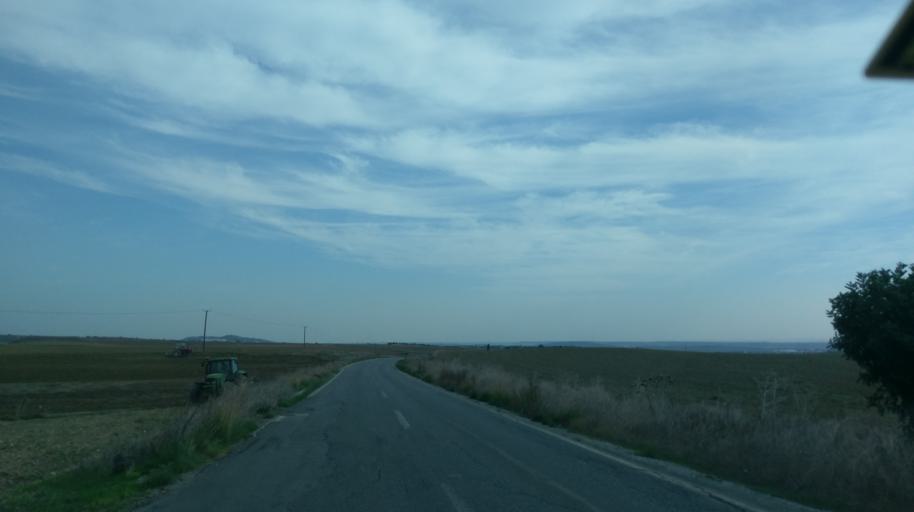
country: CY
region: Keryneia
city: Lapithos
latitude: 35.2505
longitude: 33.1487
